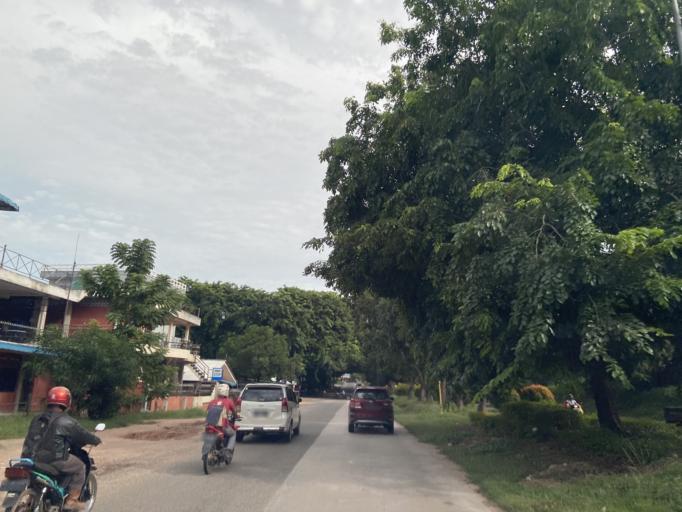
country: SG
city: Singapore
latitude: 1.1330
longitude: 104.0053
